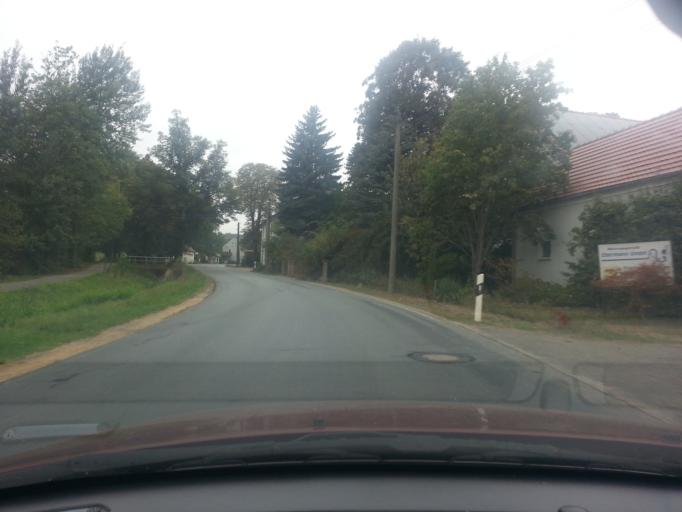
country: DE
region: Saxony
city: Schonau-Berzdorf
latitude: 51.0977
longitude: 14.8742
